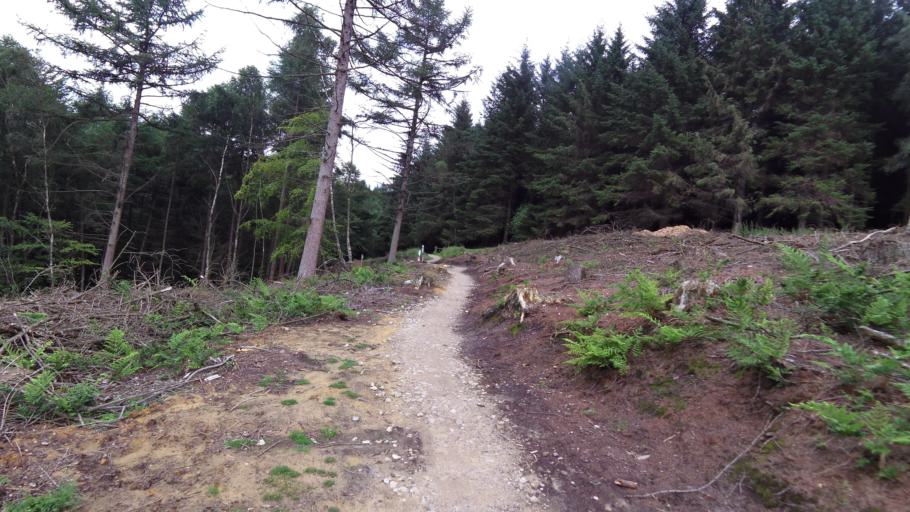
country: GB
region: England
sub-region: North Yorkshire
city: Thornton Dale
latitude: 54.2791
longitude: -0.6852
